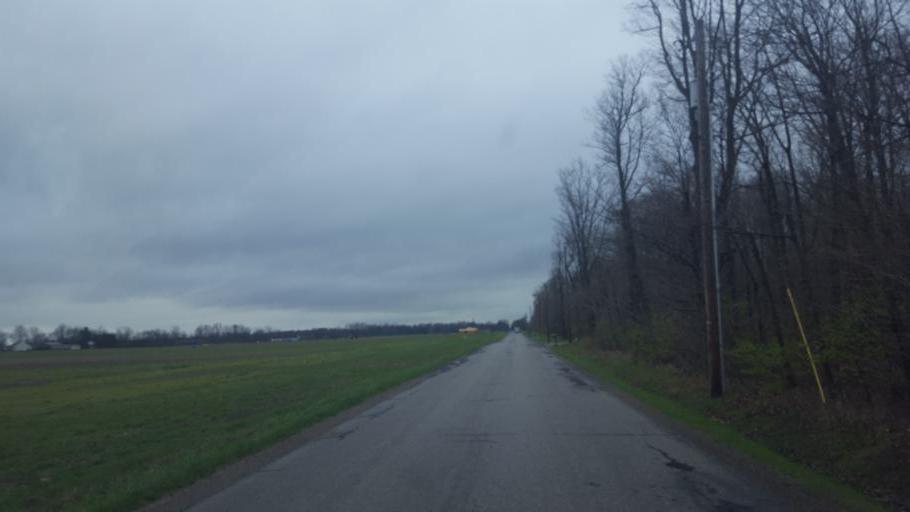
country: US
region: Ohio
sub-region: Morrow County
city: Mount Gilead
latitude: 40.5358
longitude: -82.8633
